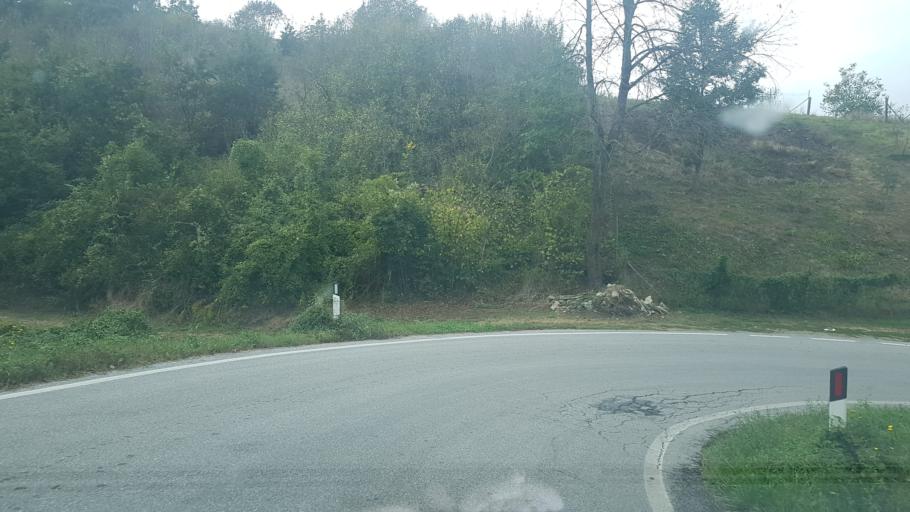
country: IT
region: Piedmont
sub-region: Provincia di Cuneo
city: Camerana
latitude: 44.4356
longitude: 8.1495
